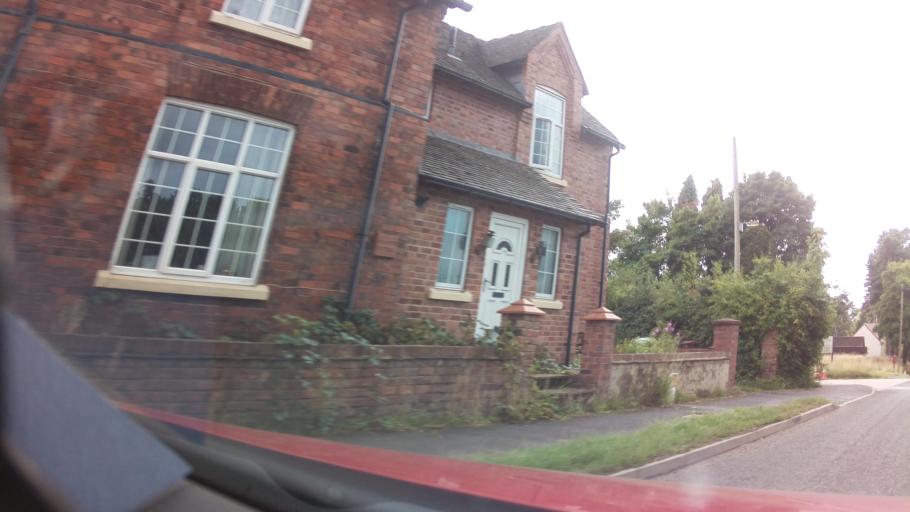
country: GB
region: England
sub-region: Staffordshire
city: Eccleshall
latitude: 52.8917
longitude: -2.2177
